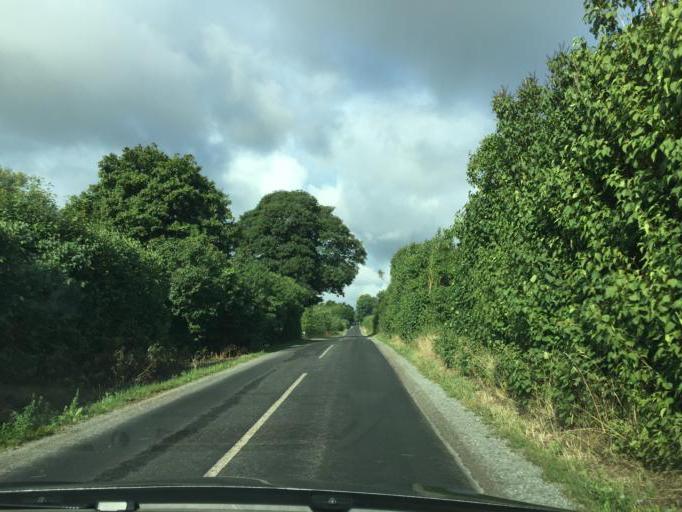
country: DK
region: South Denmark
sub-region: Faaborg-Midtfyn Kommune
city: Faaborg
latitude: 55.1928
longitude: 10.2280
